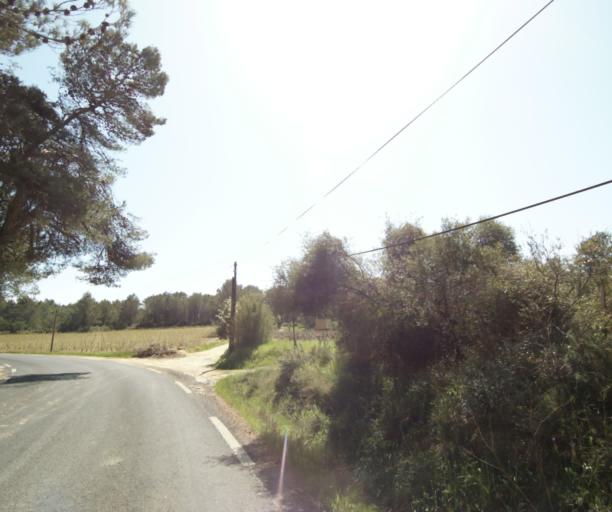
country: FR
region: Languedoc-Roussillon
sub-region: Departement de l'Herault
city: Prades-le-Lez
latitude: 43.6894
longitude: 3.8834
